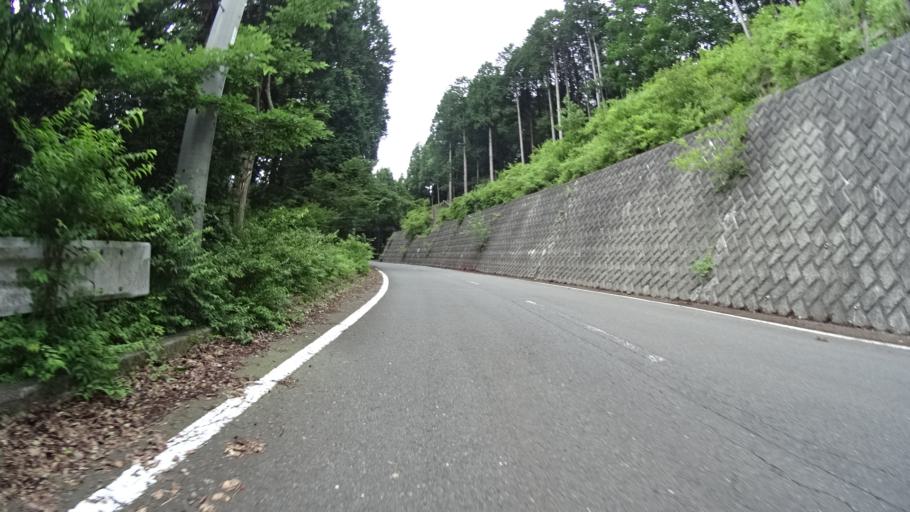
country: JP
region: Kanagawa
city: Hadano
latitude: 35.4331
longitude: 139.2108
